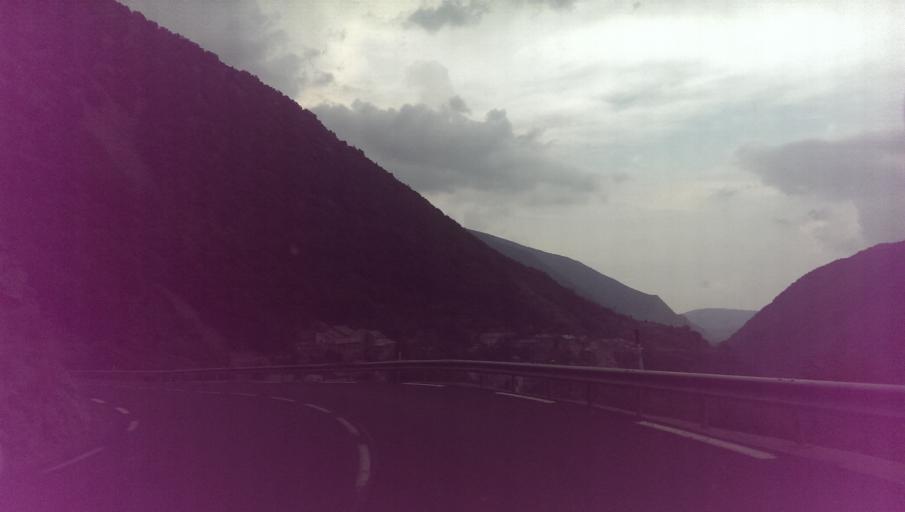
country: ES
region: Catalonia
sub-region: Provincia de Girona
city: Llivia
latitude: 42.5093
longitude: 2.1757
